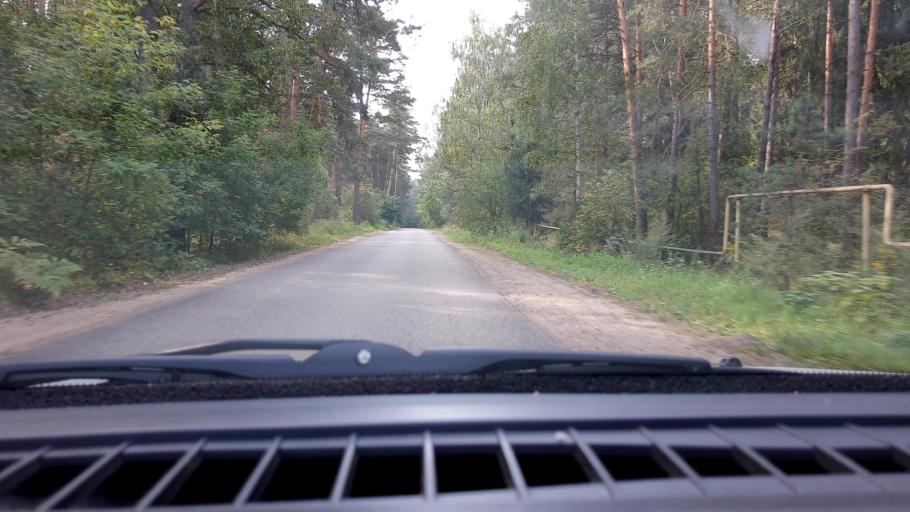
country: RU
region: Nizjnij Novgorod
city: Afonino
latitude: 56.1844
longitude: 44.0799
